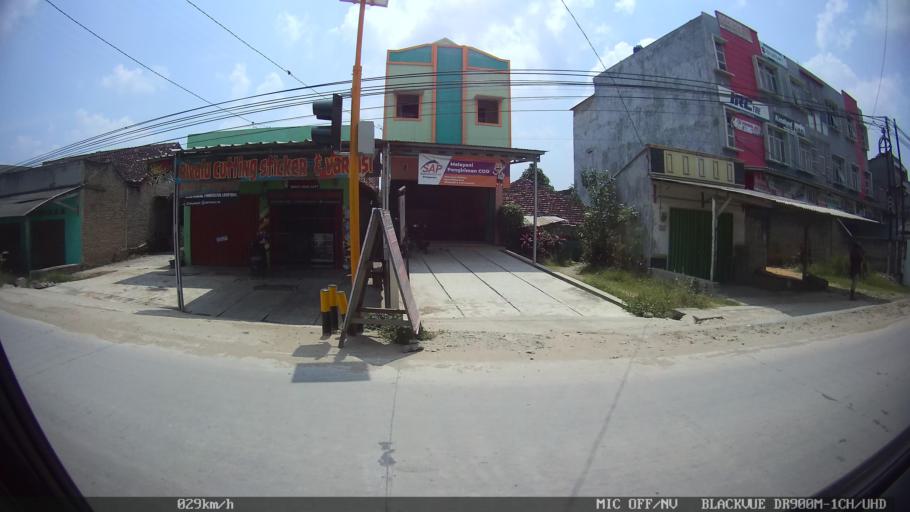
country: ID
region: Lampung
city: Pringsewu
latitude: -5.3462
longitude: 104.9753
